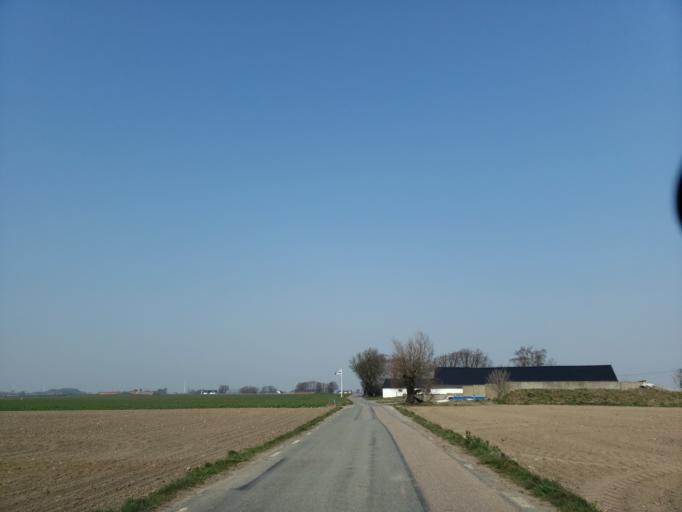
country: SE
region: Skane
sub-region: Simrishamns Kommun
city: Simrishamn
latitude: 55.4452
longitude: 14.2185
